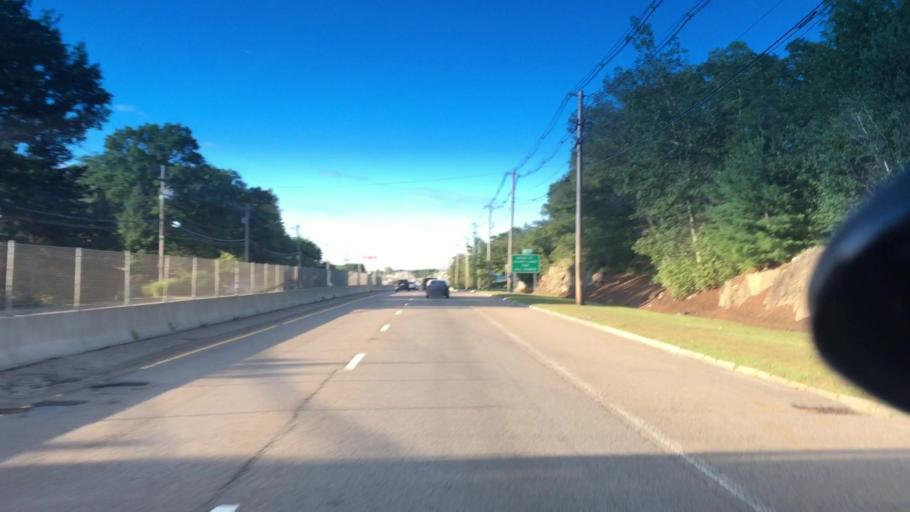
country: US
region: Massachusetts
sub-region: Norfolk County
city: Norwood
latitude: 42.1749
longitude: -71.1934
